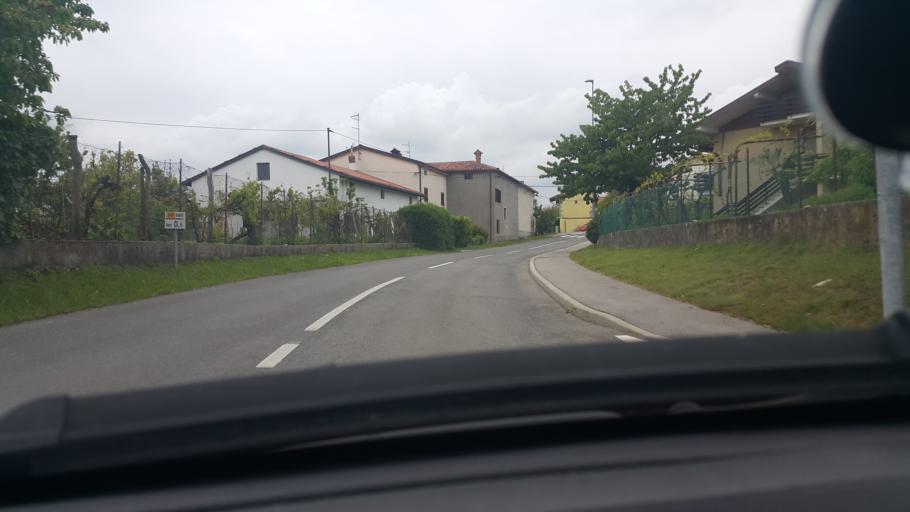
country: SI
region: Komen
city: Komen
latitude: 45.8140
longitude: 13.7505
